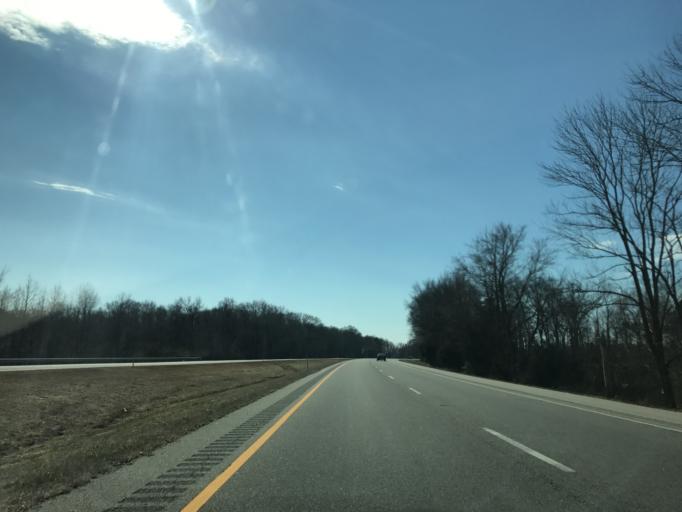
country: US
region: Maryland
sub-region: Queen Anne's County
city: Centreville
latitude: 39.1086
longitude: -75.9507
